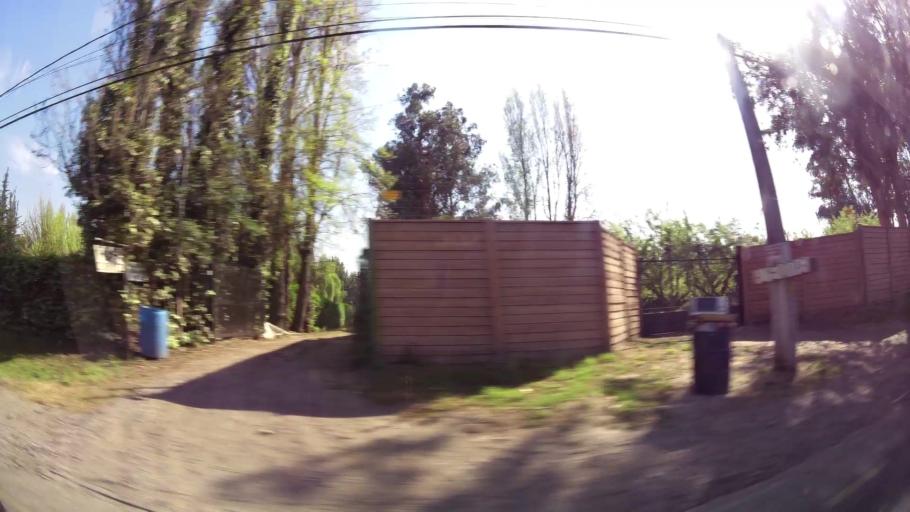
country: CL
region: Santiago Metropolitan
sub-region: Provincia de Talagante
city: Penaflor
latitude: -33.5529
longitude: -70.8338
